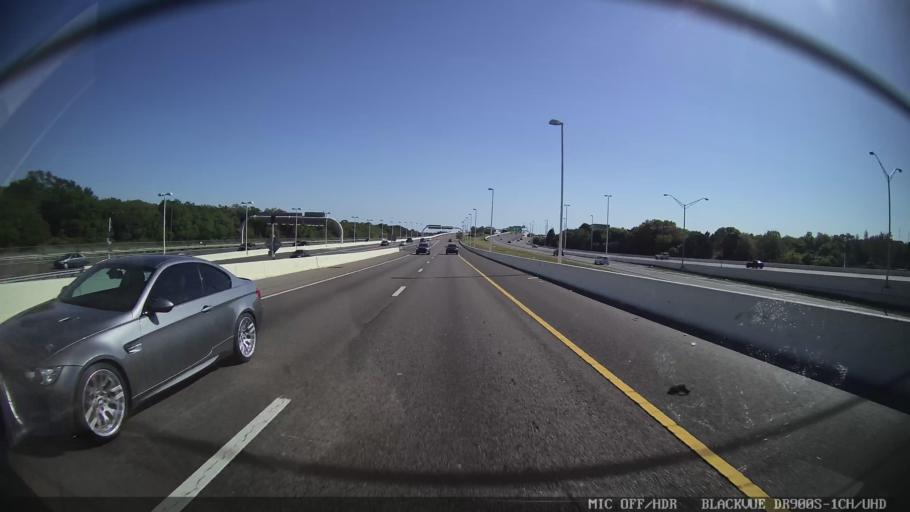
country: US
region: Florida
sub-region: Hillsborough County
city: Town 'n' Country
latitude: 27.9740
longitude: -82.5455
